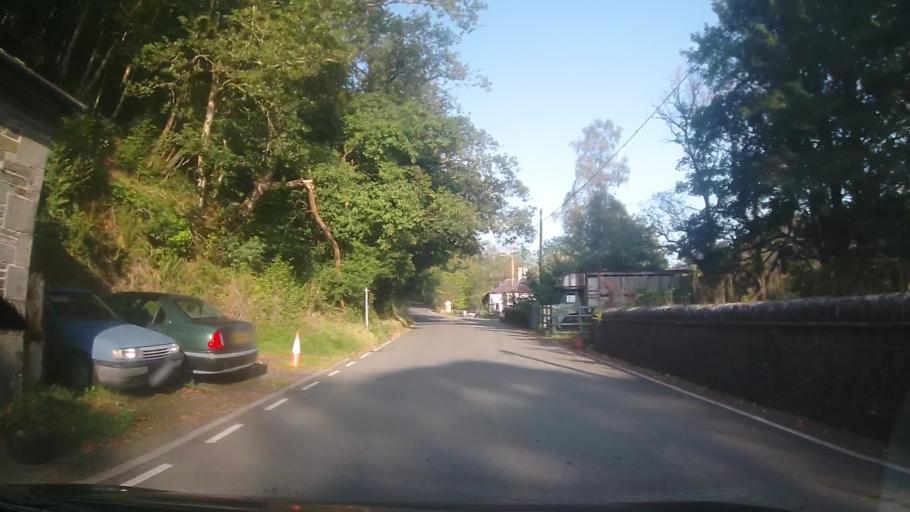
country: GB
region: Wales
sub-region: County of Ceredigion
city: Lledrod
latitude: 52.3386
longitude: -3.8481
